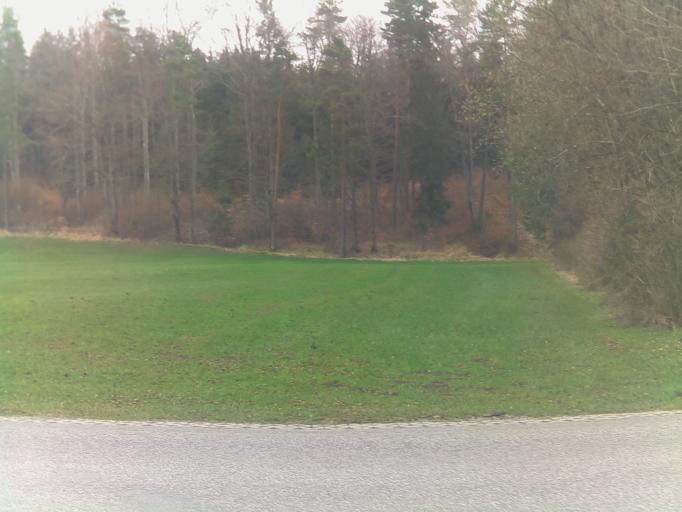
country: DE
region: Bavaria
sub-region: Upper Bavaria
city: Bernried
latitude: 47.8518
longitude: 11.2313
